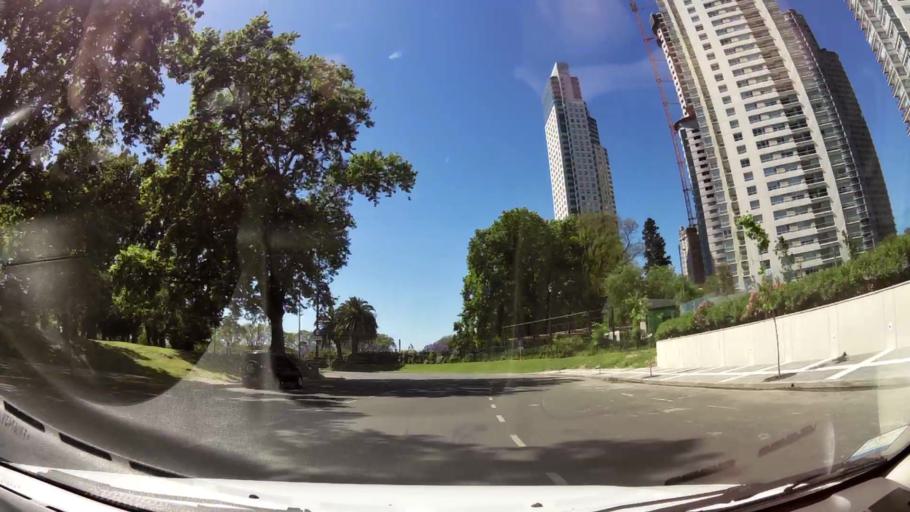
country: AR
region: Buenos Aires F.D.
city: Buenos Aires
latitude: -34.6103
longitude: -58.3605
